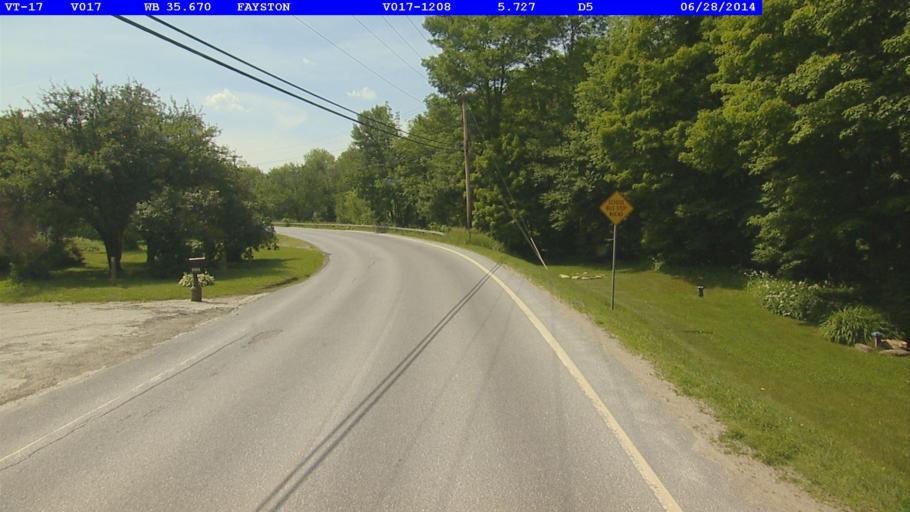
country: US
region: Vermont
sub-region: Washington County
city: Waterbury
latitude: 44.1821
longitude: -72.8450
